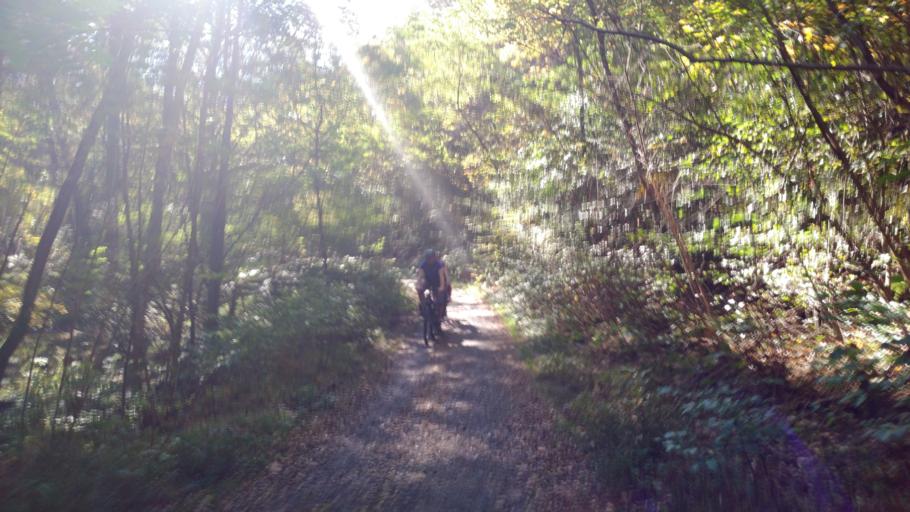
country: DE
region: Saxony
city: Albertstadt
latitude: 51.0868
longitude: 13.7725
